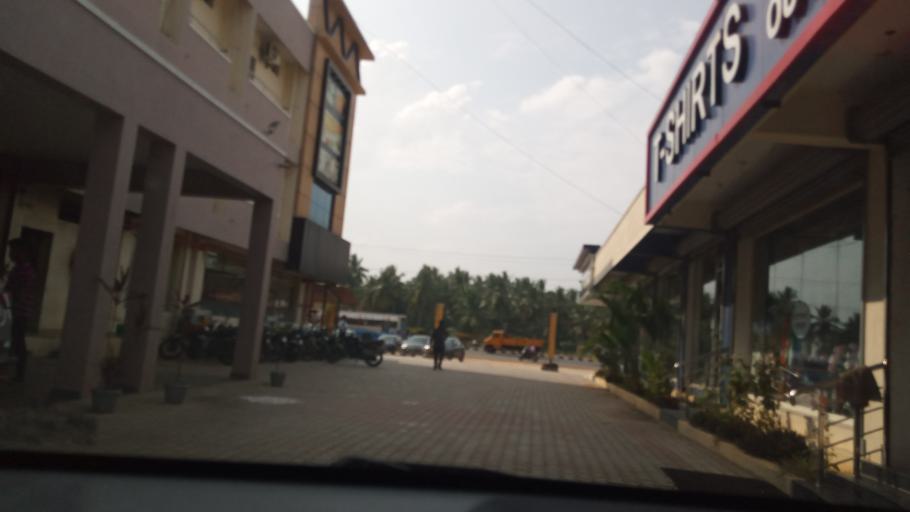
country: IN
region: Tamil Nadu
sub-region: Vellore
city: Vaniyambadi
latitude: 12.7053
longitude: 78.6486
